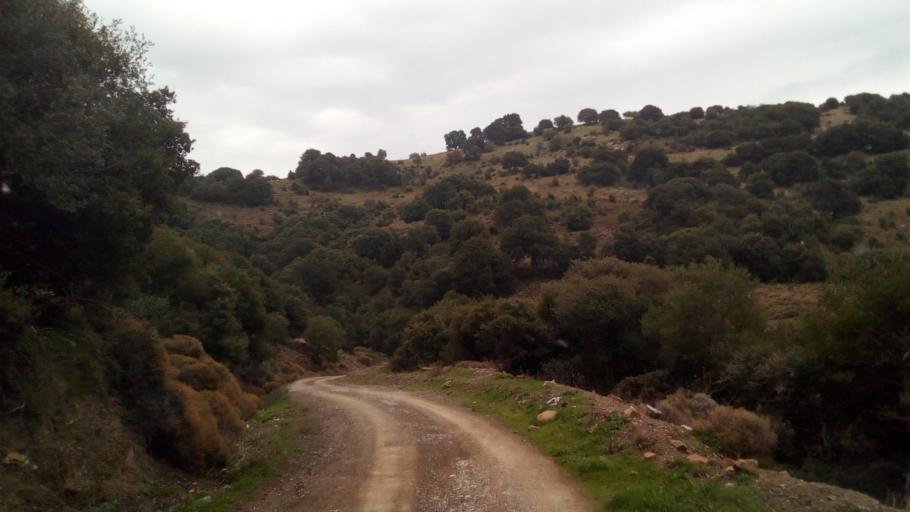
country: GR
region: West Greece
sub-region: Nomos Achaias
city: Selianitika
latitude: 38.4035
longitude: 22.0867
